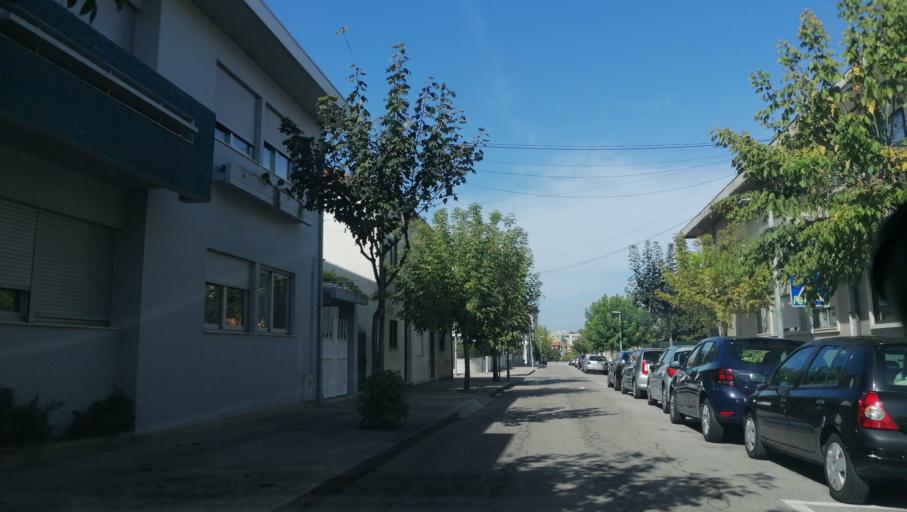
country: PT
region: Aveiro
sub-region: Espinho
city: Espinho
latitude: 41.0107
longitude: -8.6362
